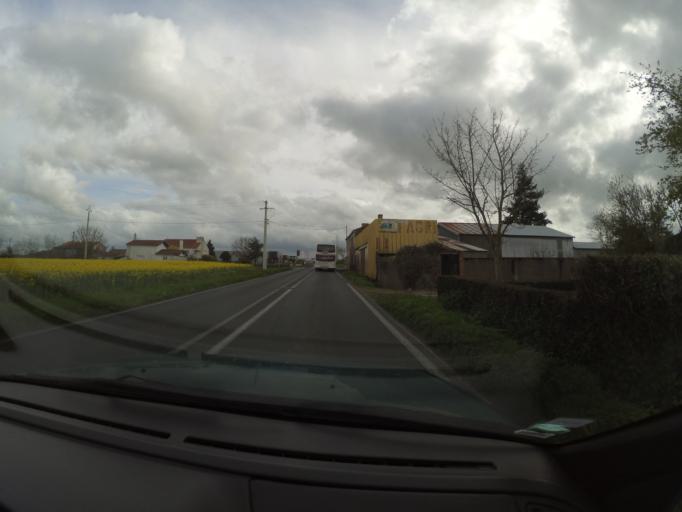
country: FR
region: Pays de la Loire
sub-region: Departement de Maine-et-Loire
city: Lire
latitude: 47.3268
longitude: -1.1667
